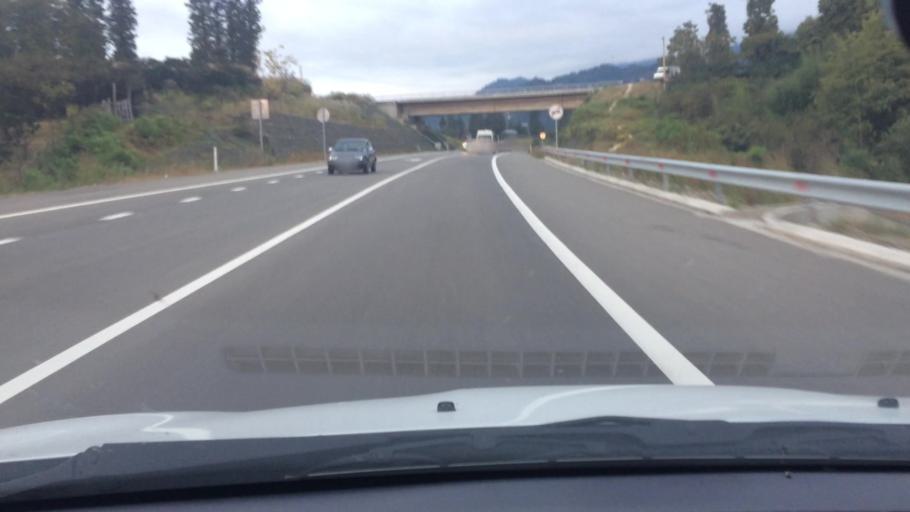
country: GE
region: Ajaria
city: Makhinjauri
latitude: 41.7061
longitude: 41.7406
